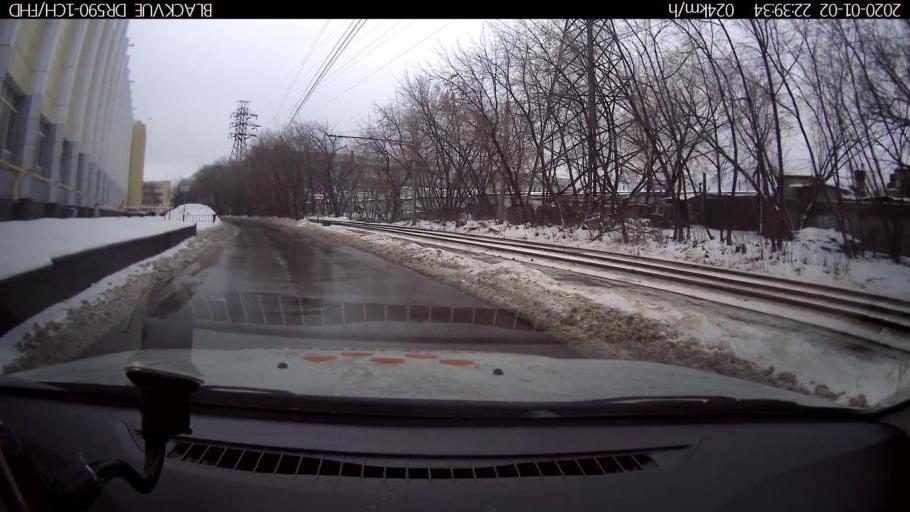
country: RU
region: Nizjnij Novgorod
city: Nizhniy Novgorod
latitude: 56.3320
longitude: 43.9029
